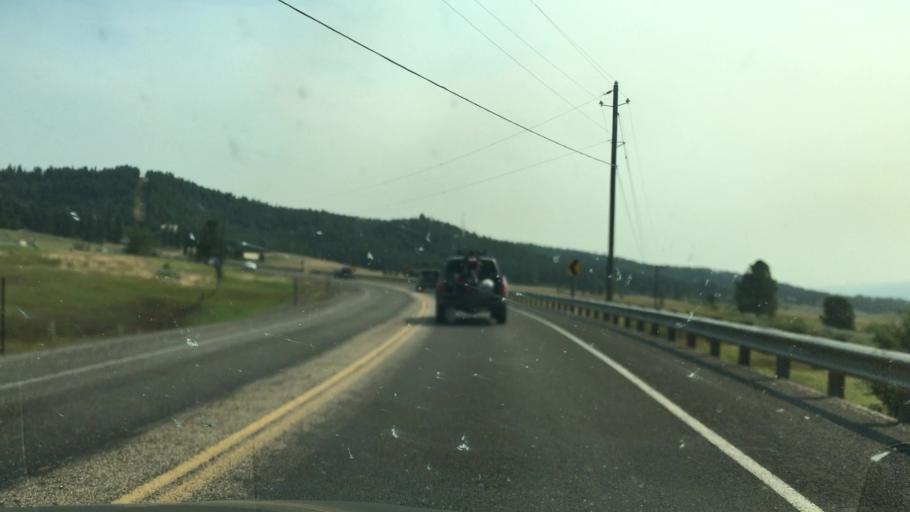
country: US
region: Idaho
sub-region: Valley County
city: Cascade
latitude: 44.5996
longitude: -116.0484
